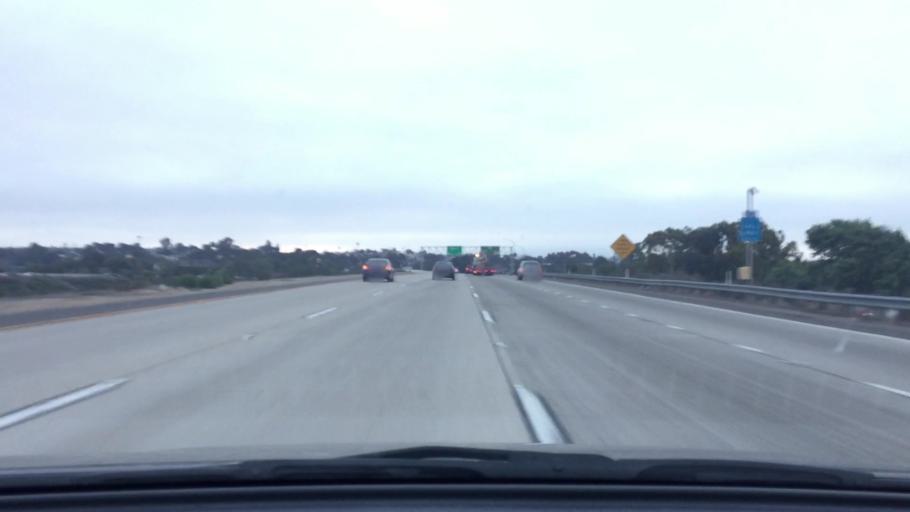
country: US
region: California
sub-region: San Diego County
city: Chula Vista
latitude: 32.6568
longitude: -117.0846
